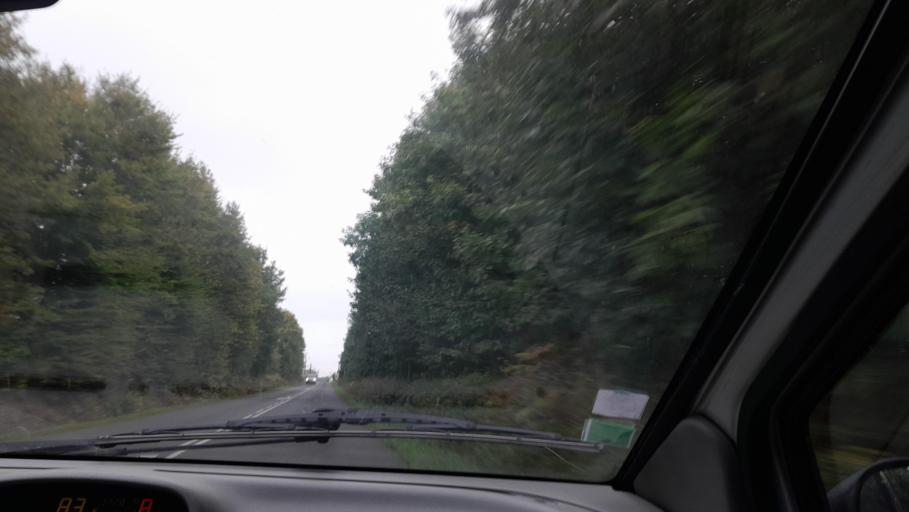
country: FR
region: Pays de la Loire
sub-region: Departement de Maine-et-Loire
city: Pouance
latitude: 47.7120
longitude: -1.1785
